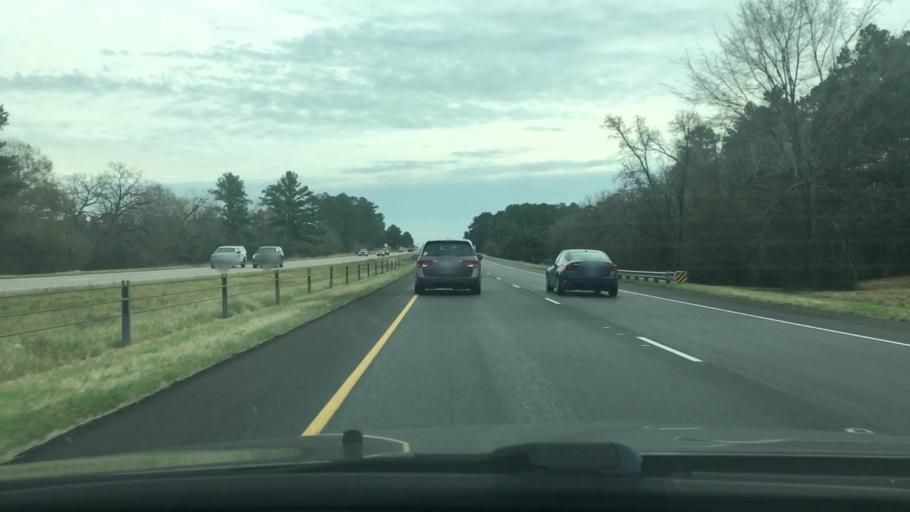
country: US
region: Texas
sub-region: Madison County
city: Madisonville
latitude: 30.8856
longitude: -95.7702
